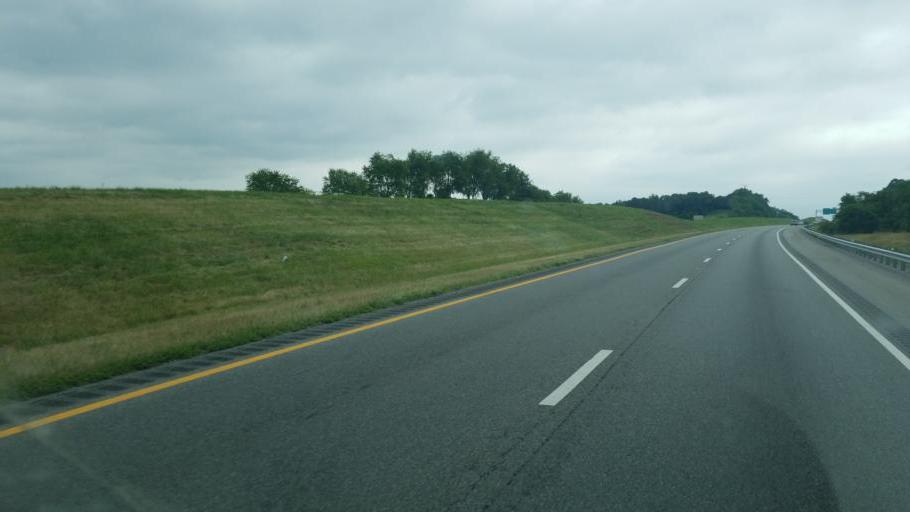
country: US
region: Virginia
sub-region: Wythe County
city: Wytheville
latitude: 36.9324
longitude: -80.9118
